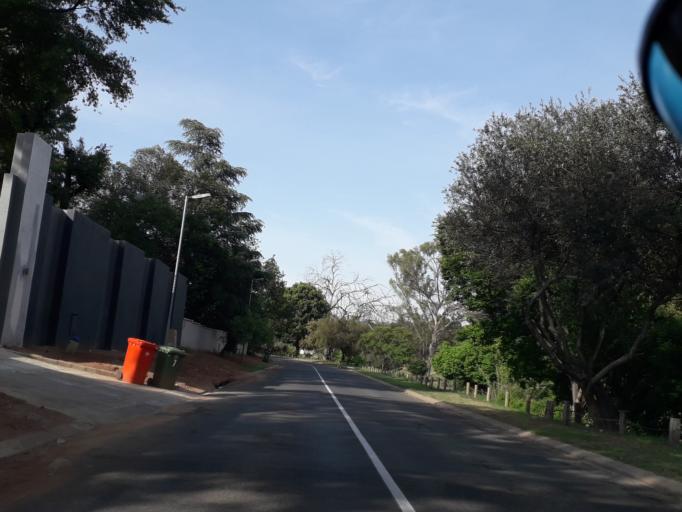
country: ZA
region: Gauteng
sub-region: City of Johannesburg Metropolitan Municipality
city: Midrand
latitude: -26.0685
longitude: 28.0394
